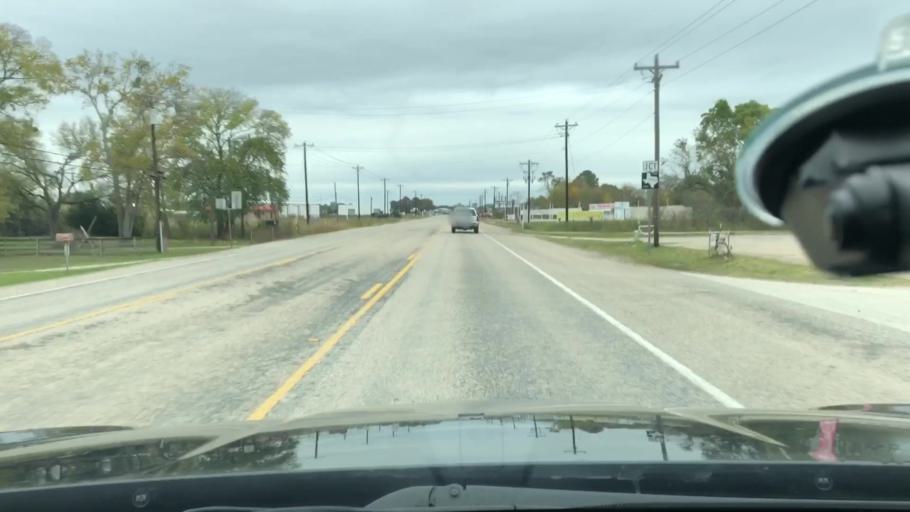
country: US
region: Texas
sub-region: Hunt County
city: Greenville
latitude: 33.0366
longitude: -96.1070
